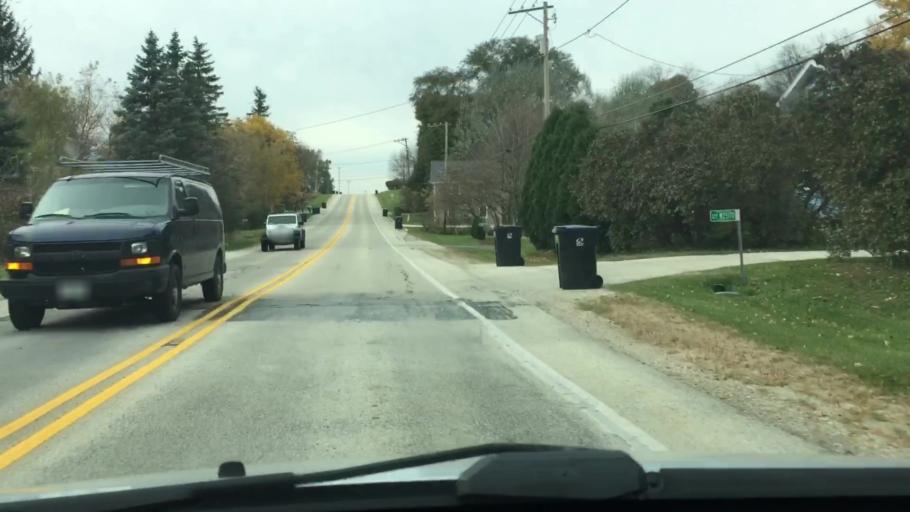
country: US
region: Wisconsin
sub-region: Waukesha County
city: Big Bend
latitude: 42.9041
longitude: -88.2515
